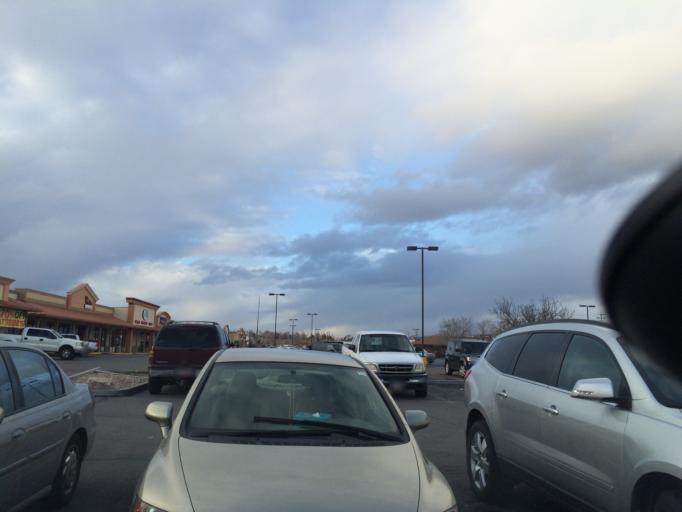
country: US
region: Utah
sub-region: Salt Lake County
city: West Jordan
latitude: 40.6212
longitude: -111.9399
